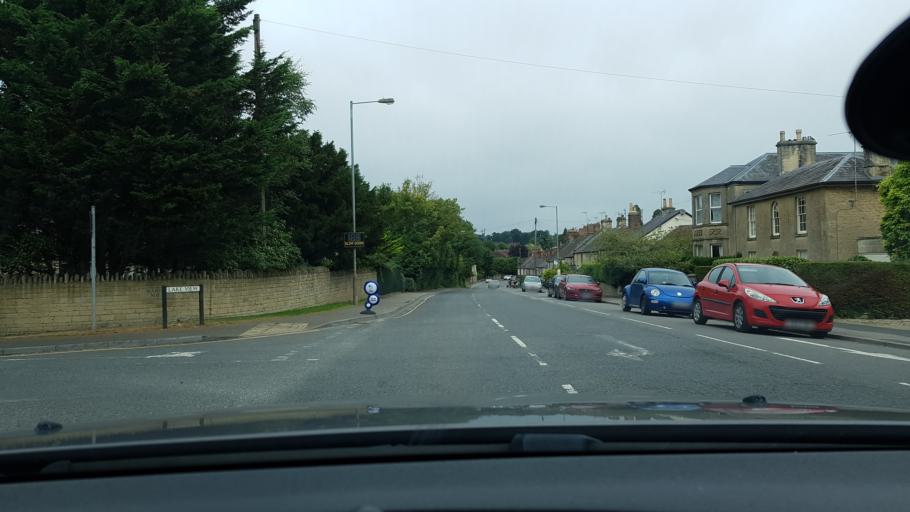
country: GB
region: England
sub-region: Wiltshire
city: Calne
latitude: 51.4265
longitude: -1.9894
